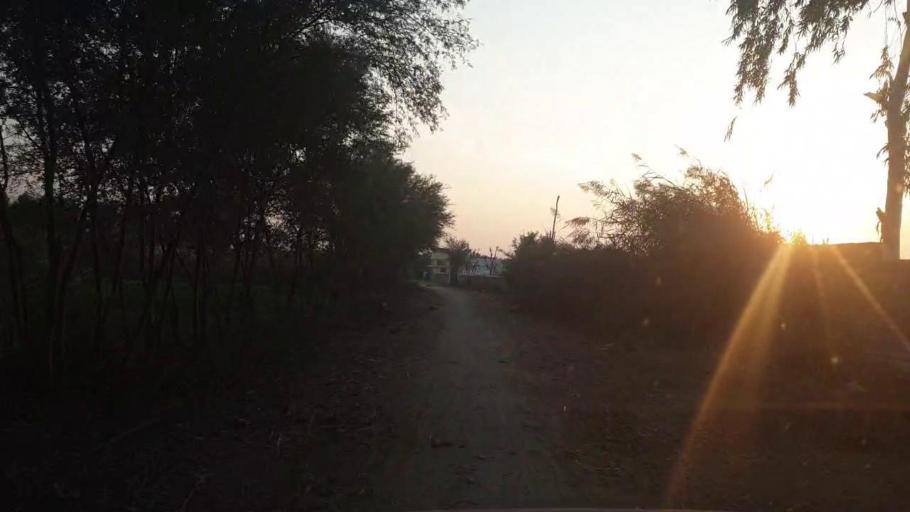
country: PK
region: Sindh
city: Bhit Shah
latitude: 25.8688
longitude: 68.5360
